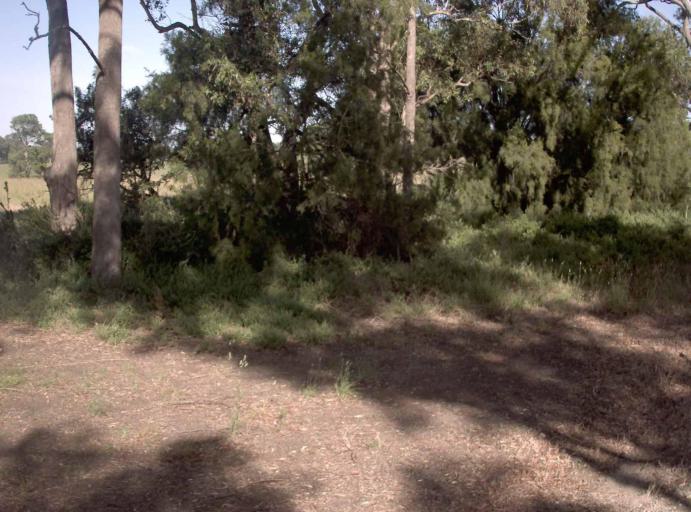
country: AU
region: Victoria
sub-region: East Gippsland
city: Lakes Entrance
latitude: -37.8101
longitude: 147.8446
